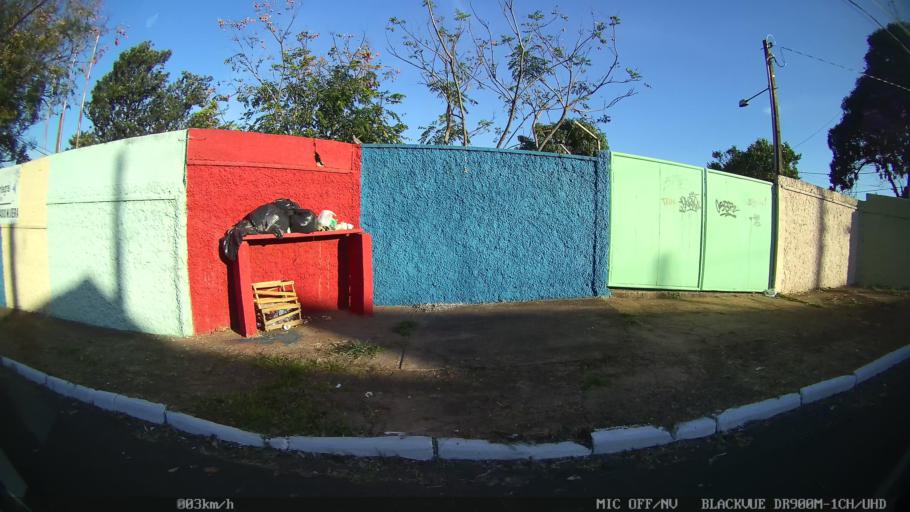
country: BR
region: Sao Paulo
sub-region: Franca
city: Franca
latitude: -20.5319
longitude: -47.3779
